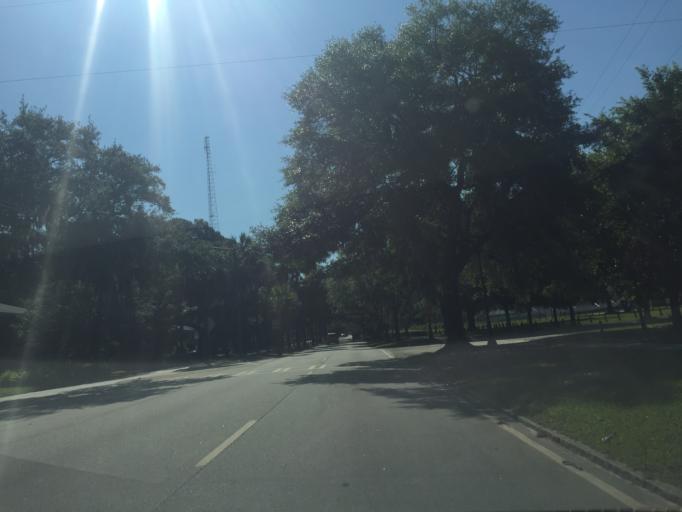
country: US
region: Georgia
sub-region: Chatham County
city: Thunderbolt
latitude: 32.0473
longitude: -81.0819
